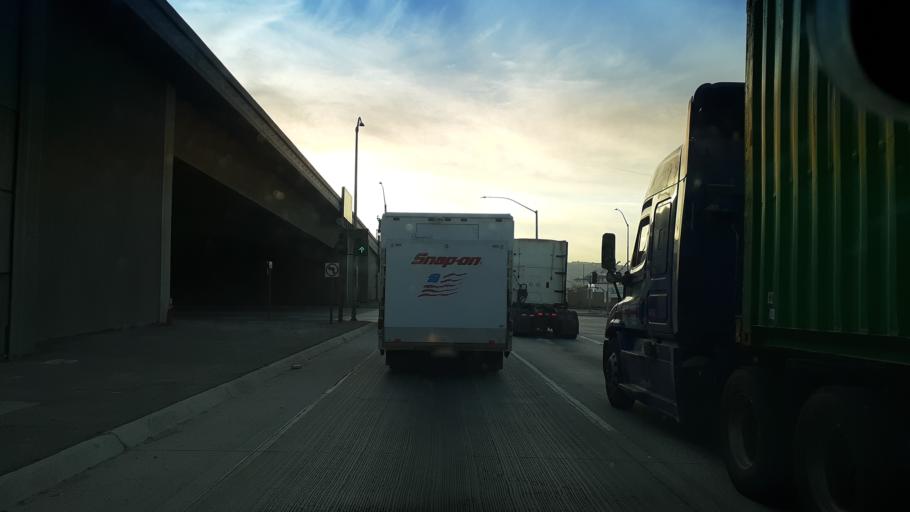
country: US
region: California
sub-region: Los Angeles County
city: Long Beach
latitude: 33.7582
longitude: -118.2402
